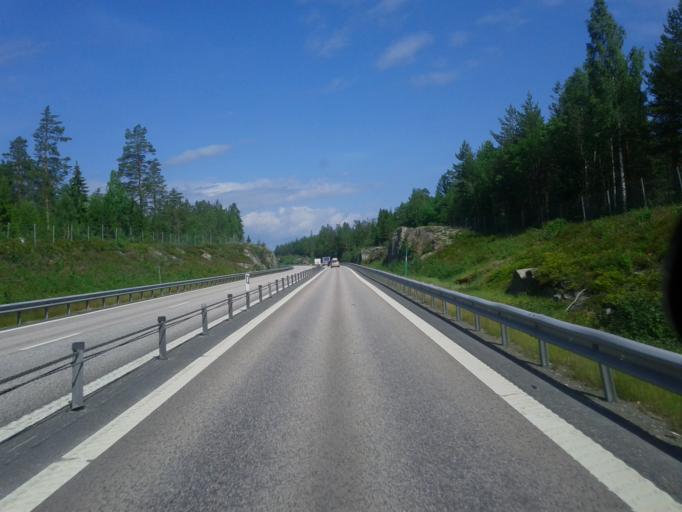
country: SE
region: Vaesternorrland
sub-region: OErnskoeldsviks Kommun
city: Husum
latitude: 63.3842
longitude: 19.1934
